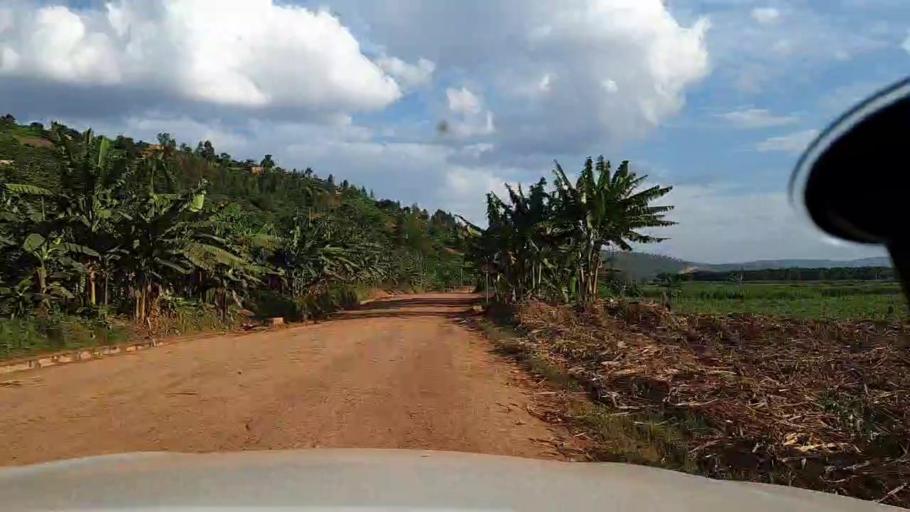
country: RW
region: Kigali
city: Kigali
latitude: -1.9323
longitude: 29.9961
